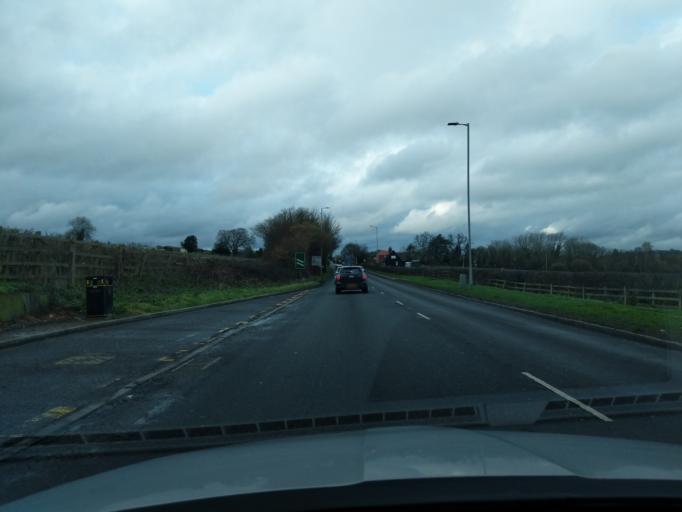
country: GB
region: England
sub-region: Hertfordshire
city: Kings Langley
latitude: 51.7039
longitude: -0.4446
